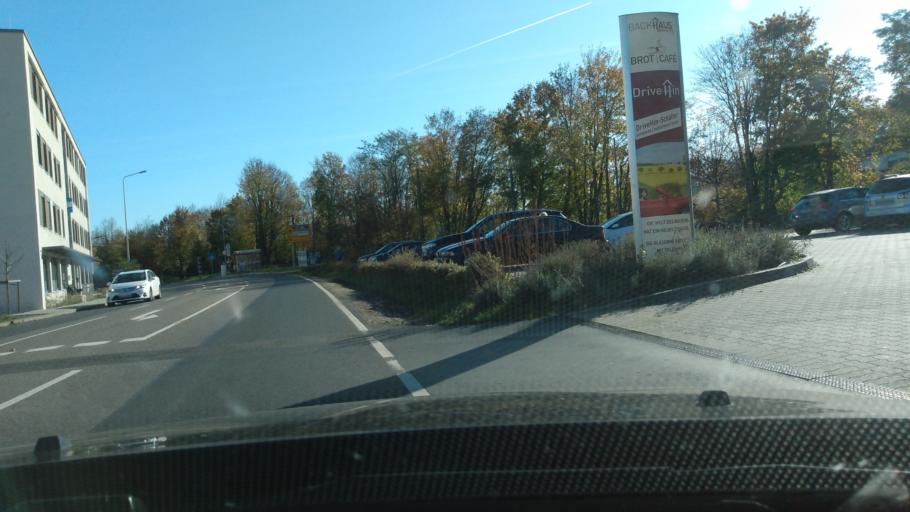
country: DE
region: Hesse
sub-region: Regierungsbezirk Darmstadt
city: Kriftel
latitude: 50.0797
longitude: 8.4608
